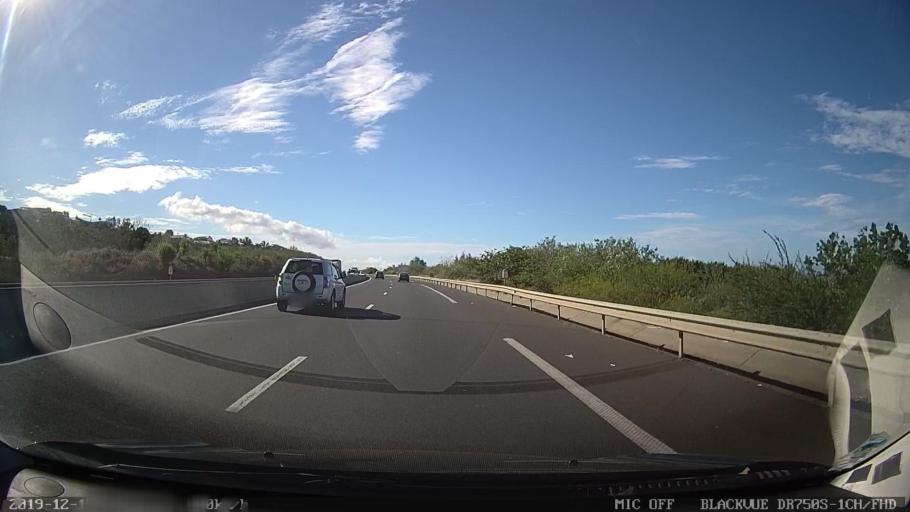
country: RE
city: Piton Saint-Leu
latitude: -21.2065
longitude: 55.2921
